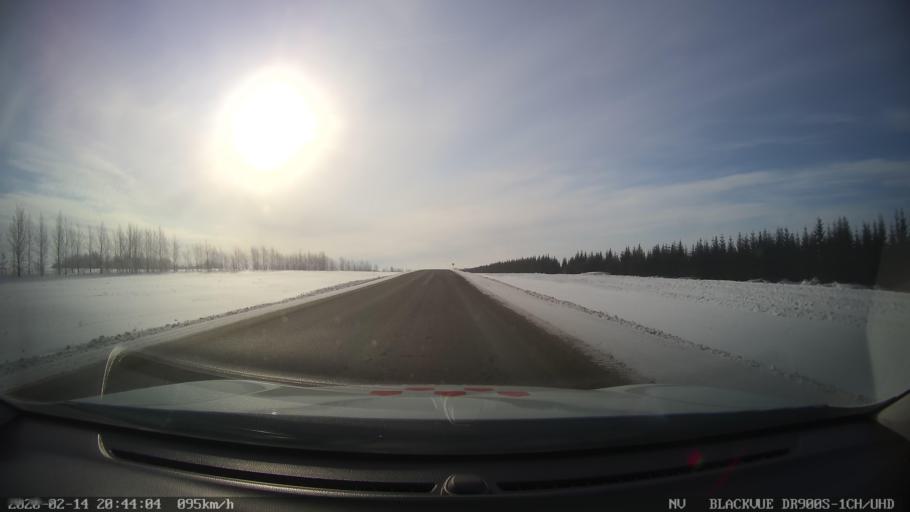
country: RU
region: Tatarstan
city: Kuybyshevskiy Zaton
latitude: 55.2993
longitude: 49.1471
